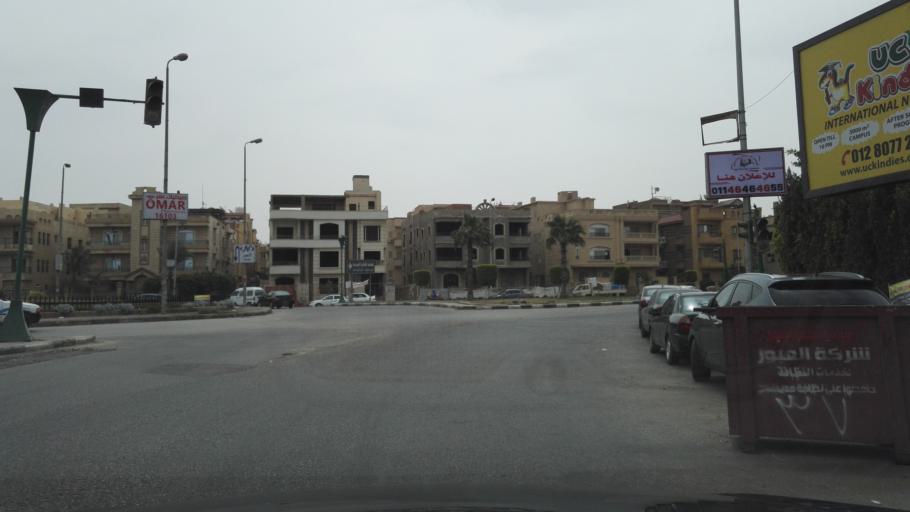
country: EG
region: Muhafazat al Qahirah
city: Cairo
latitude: 30.0021
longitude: 31.4227
